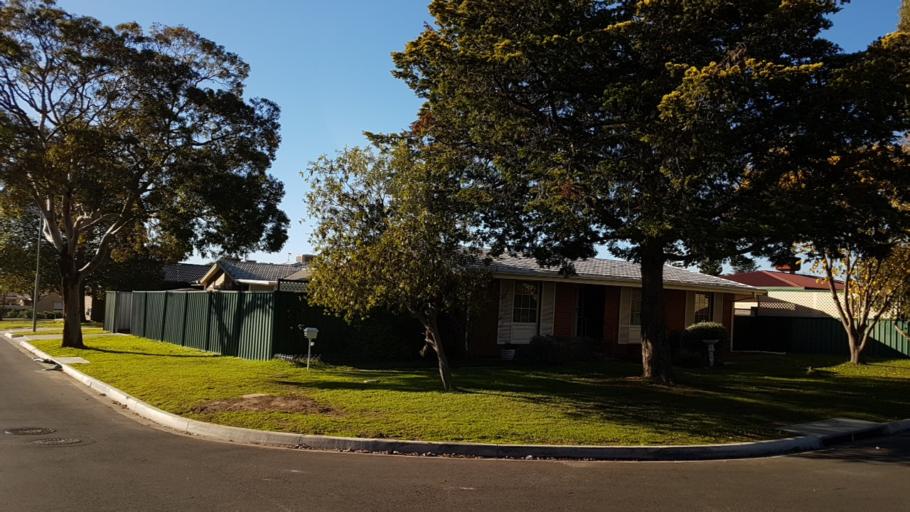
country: AU
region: South Australia
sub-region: Campbelltown
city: Campbelltown
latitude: -34.8835
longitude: 138.6832
